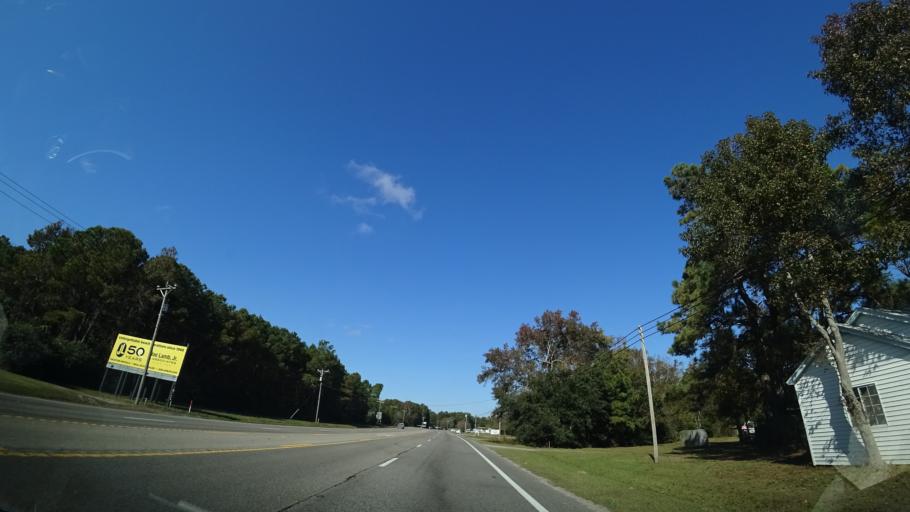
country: US
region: North Carolina
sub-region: Dare County
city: Southern Shores
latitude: 36.1782
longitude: -75.8634
